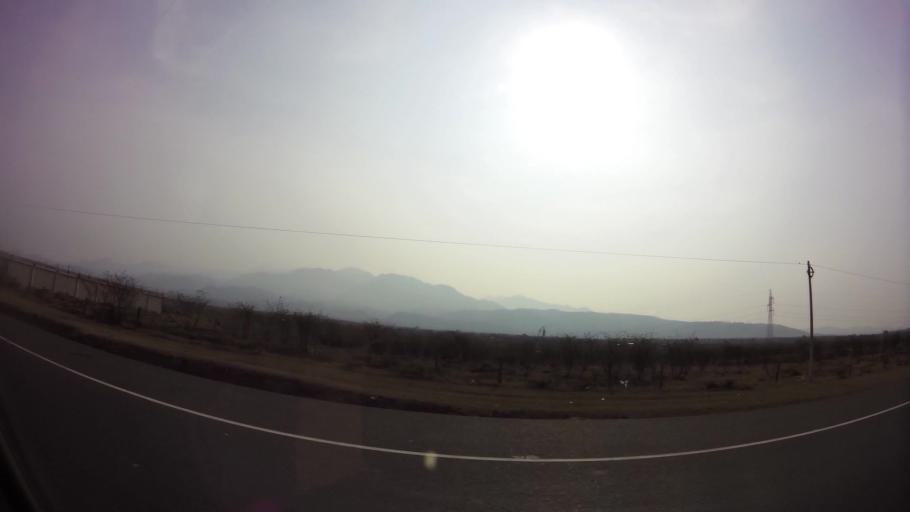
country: HN
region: Comayagua
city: Comayagua
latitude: 14.4044
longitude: -87.6198
